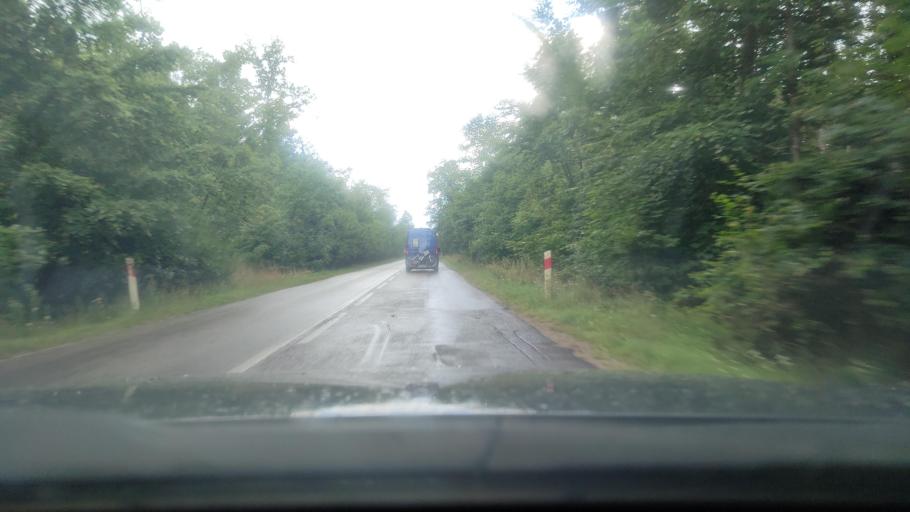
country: PL
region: Pomeranian Voivodeship
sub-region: Powiat wejherowski
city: Orle
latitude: 54.7021
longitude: 18.1743
